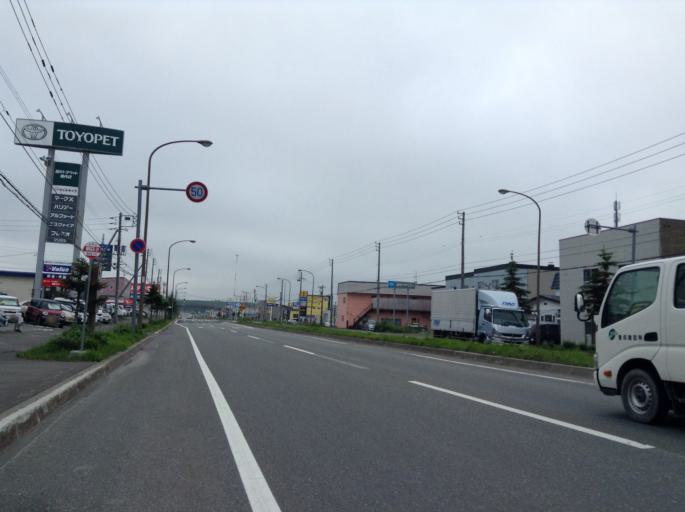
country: JP
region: Hokkaido
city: Wakkanai
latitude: 45.3845
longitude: 141.7073
